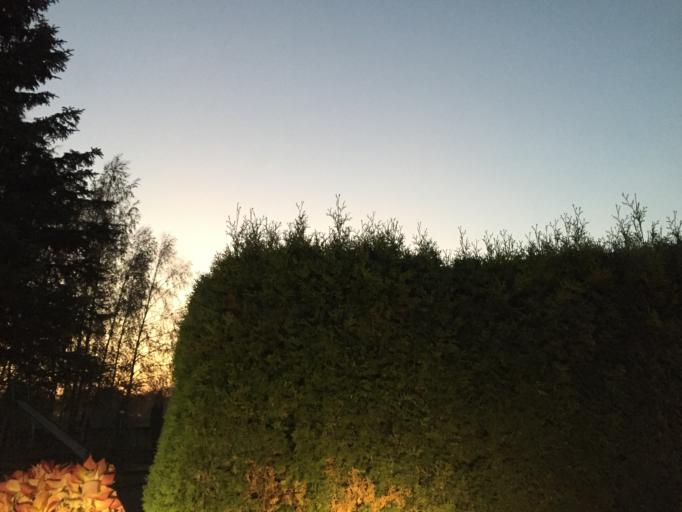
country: LT
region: Klaipedos apskritis
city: Kretinga
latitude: 55.8960
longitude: 21.2390
